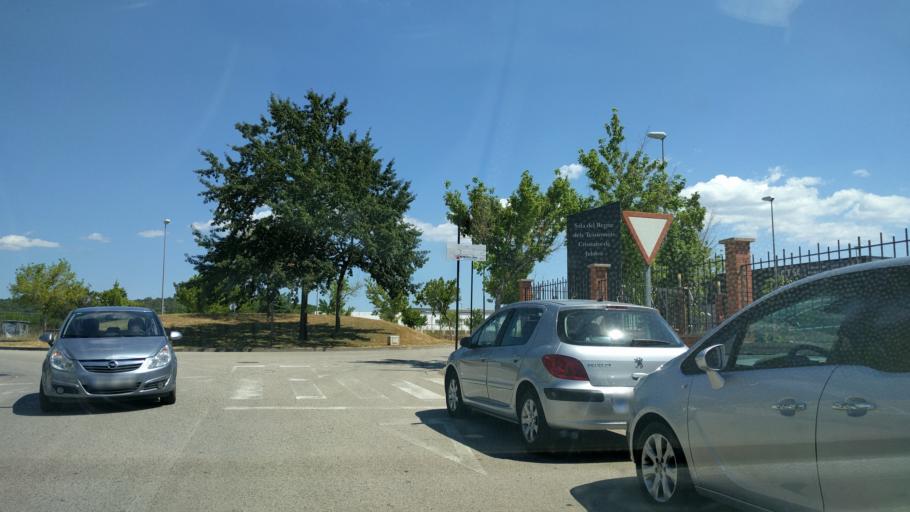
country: ES
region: Catalonia
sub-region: Provincia de Girona
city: Salt
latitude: 41.9928
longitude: 2.7955
